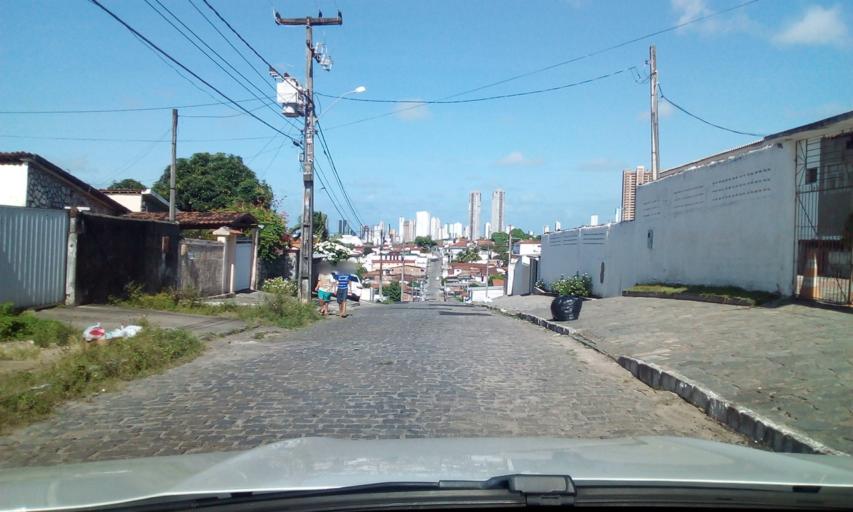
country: BR
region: Paraiba
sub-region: Joao Pessoa
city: Joao Pessoa
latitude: -7.1040
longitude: -34.8625
